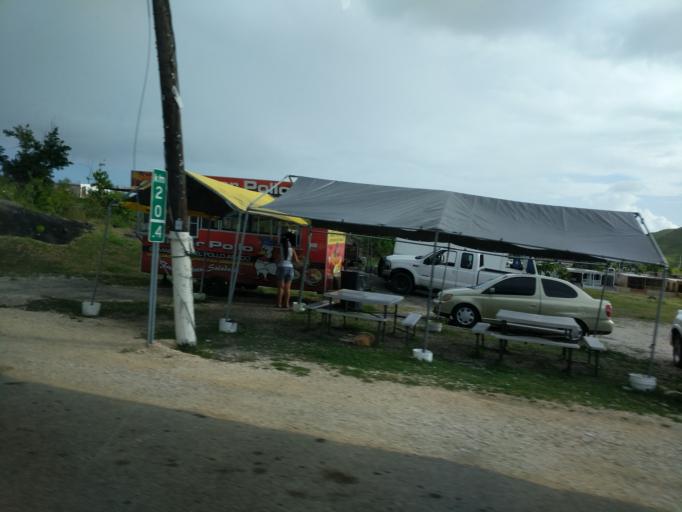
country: PR
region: Coamo
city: Coamo
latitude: 18.0793
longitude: -66.3716
